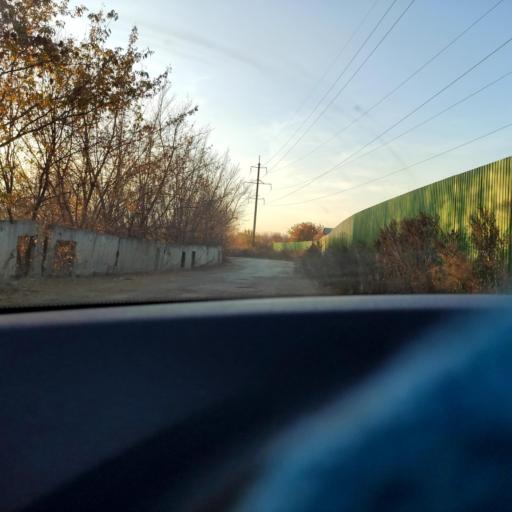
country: RU
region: Samara
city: Petra-Dubrava
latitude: 53.2610
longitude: 50.2979
